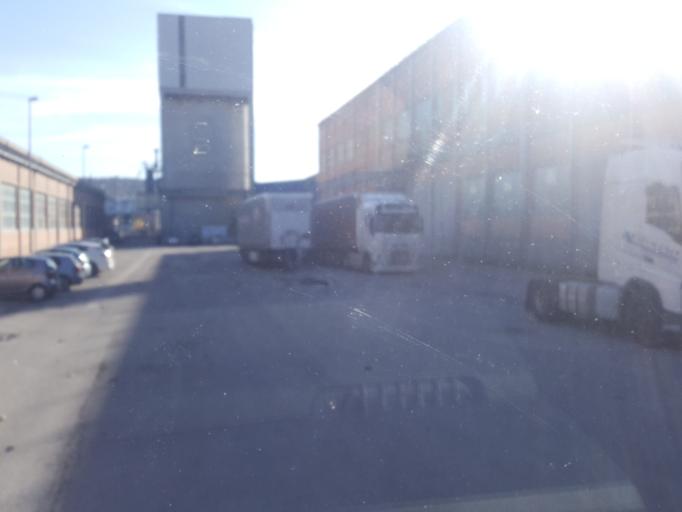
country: IT
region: Friuli Venezia Giulia
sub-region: Provincia di Trieste
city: Domio
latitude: 45.6148
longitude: 13.8056
